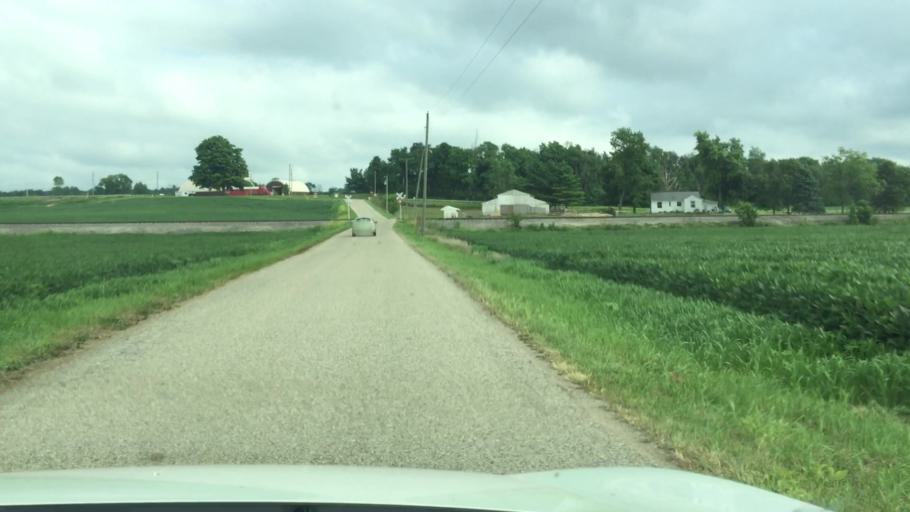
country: US
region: Ohio
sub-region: Champaign County
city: Mechanicsburg
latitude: 40.0482
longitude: -83.6335
